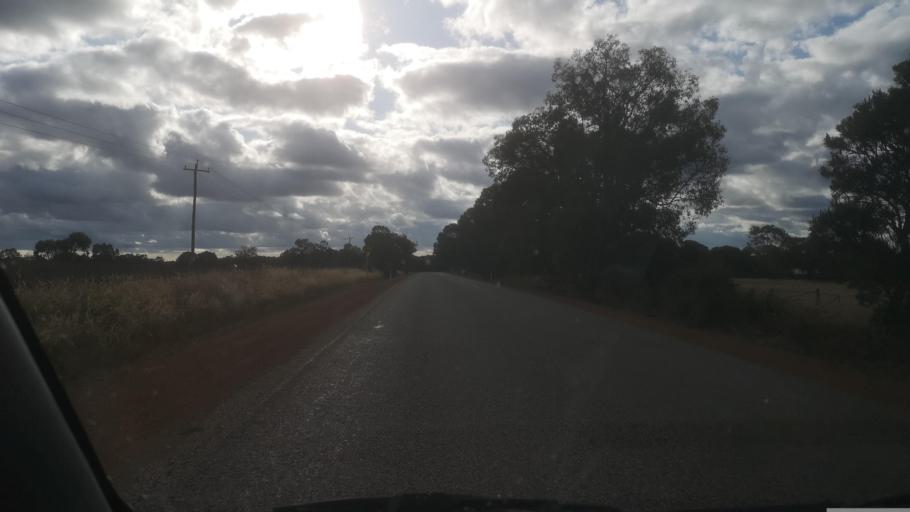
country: AU
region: Western Australia
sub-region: Chittering
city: Lower Chittering
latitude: -31.3273
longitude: 116.0305
